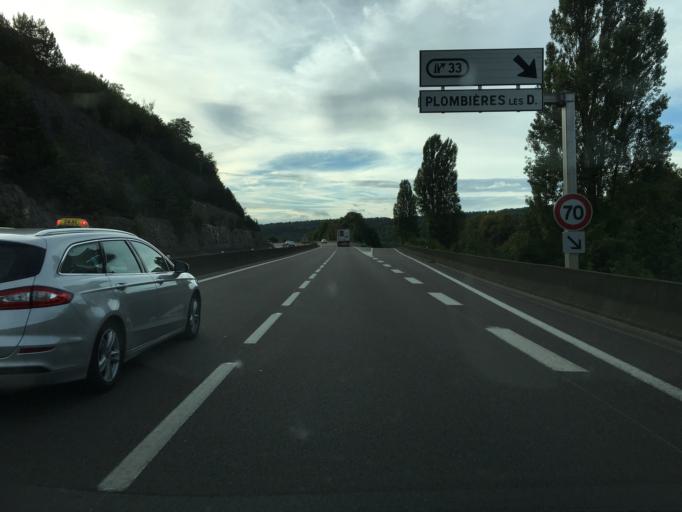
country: FR
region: Bourgogne
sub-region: Departement de la Cote-d'Or
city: Plombieres-les-Dijon
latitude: 47.3353
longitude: 4.9733
